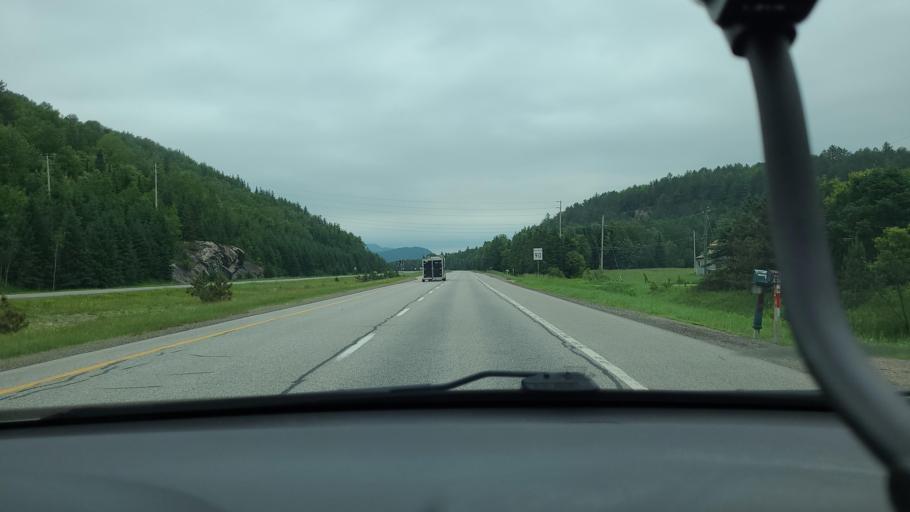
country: CA
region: Quebec
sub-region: Laurentides
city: Labelle
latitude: 46.2112
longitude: -74.7133
